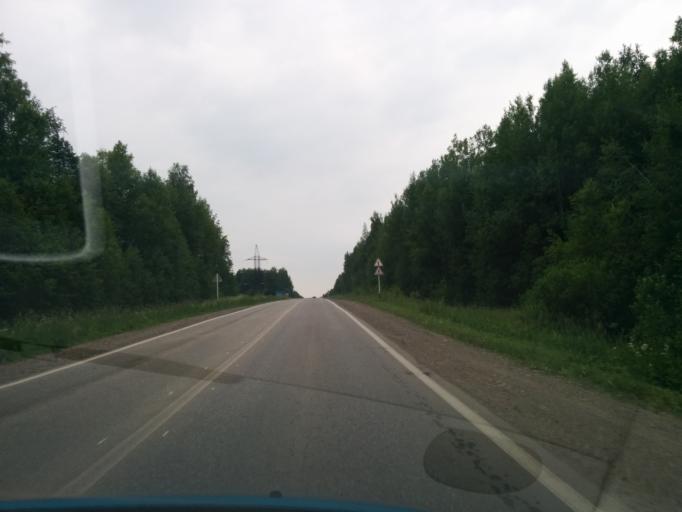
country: RU
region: Perm
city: Perm
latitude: 58.1436
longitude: 56.2651
